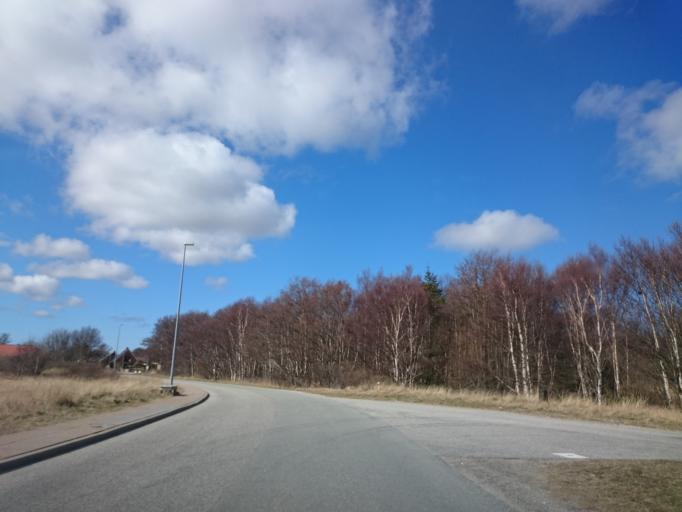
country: DK
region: North Denmark
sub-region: Frederikshavn Kommune
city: Strandby
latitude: 57.5928
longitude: 10.4249
